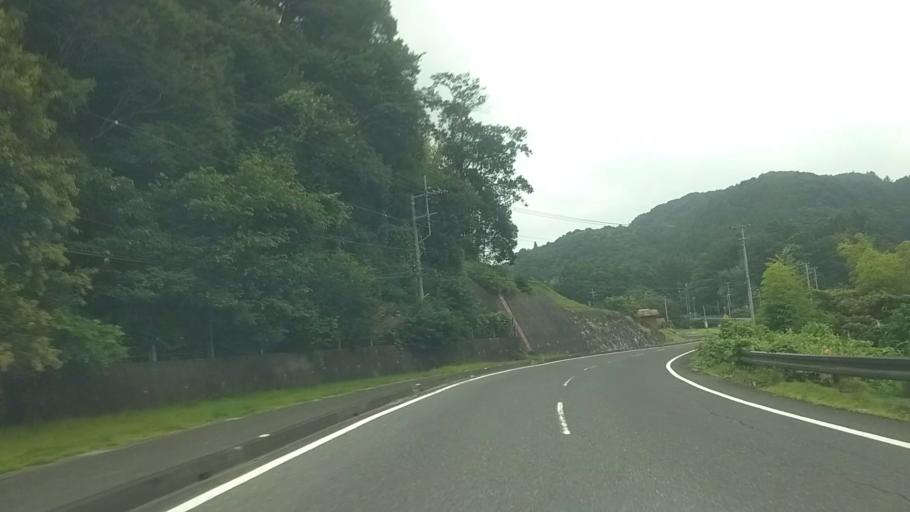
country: JP
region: Chiba
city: Kawaguchi
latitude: 35.2294
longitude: 140.1143
